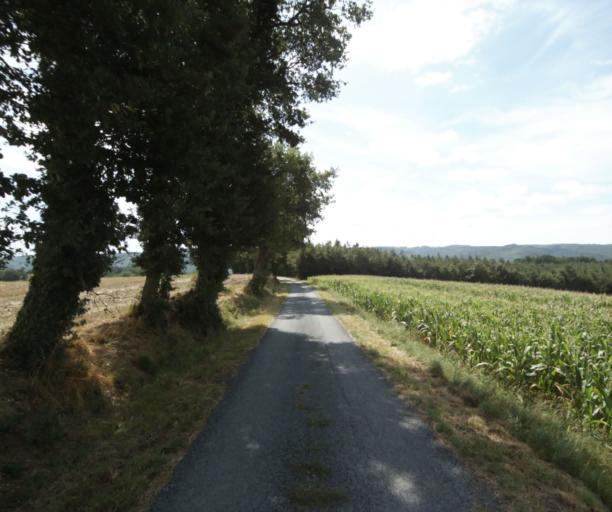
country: FR
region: Midi-Pyrenees
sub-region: Departement du Tarn
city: Dourgne
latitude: 43.4911
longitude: 2.0967
